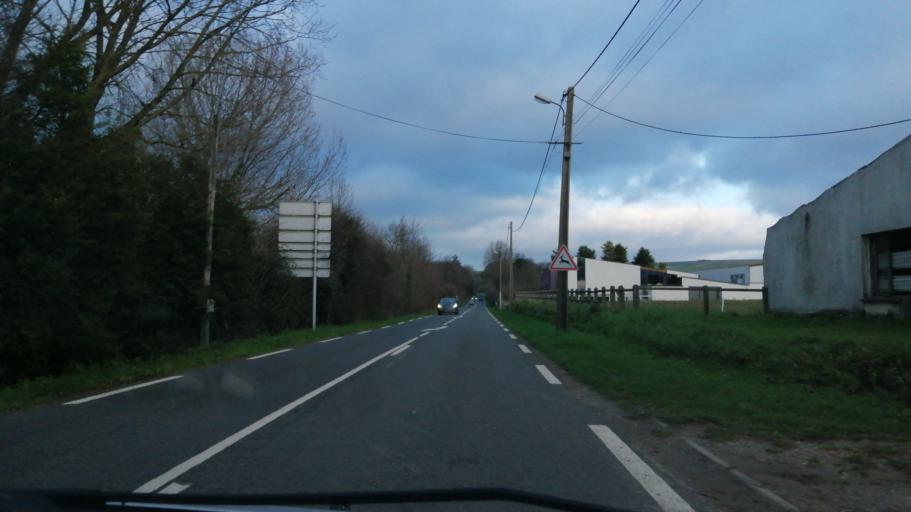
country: FR
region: Nord-Pas-de-Calais
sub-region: Departement du Pas-de-Calais
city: Wissant
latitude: 50.8896
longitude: 1.6776
